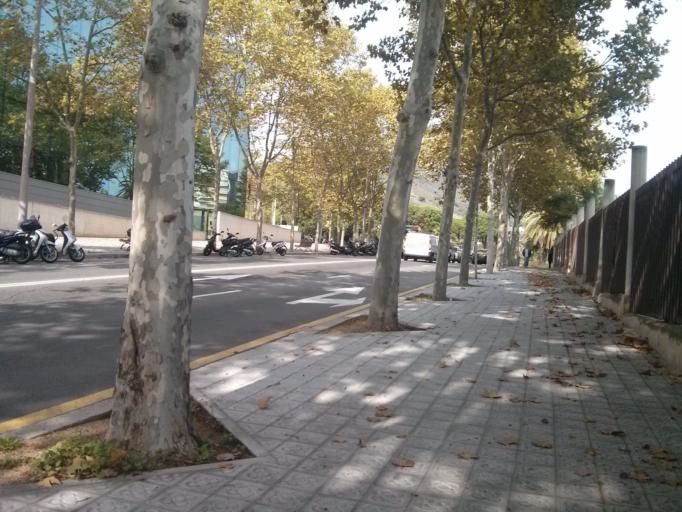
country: ES
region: Catalonia
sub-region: Provincia de Barcelona
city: Esplugues de Llobregat
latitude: 41.3822
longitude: 2.1074
